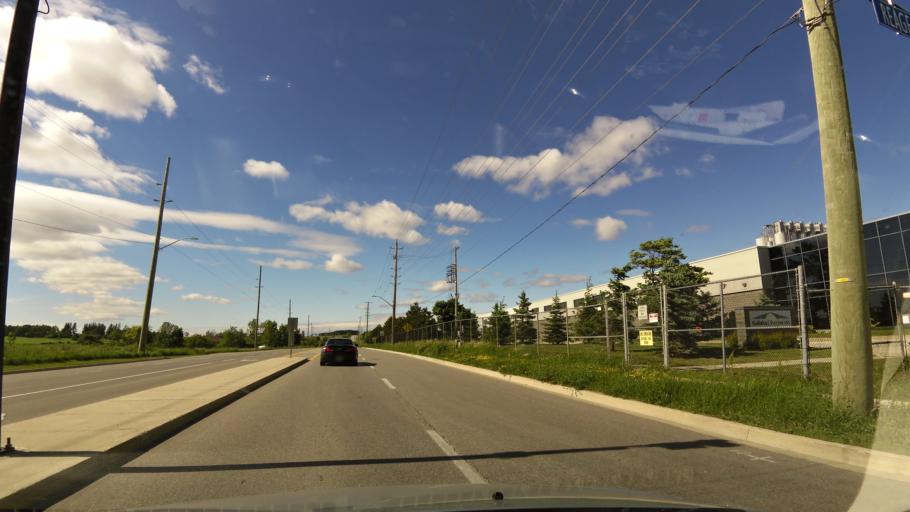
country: CA
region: Ontario
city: Bradford West Gwillimbury
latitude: 44.1115
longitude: -79.6032
